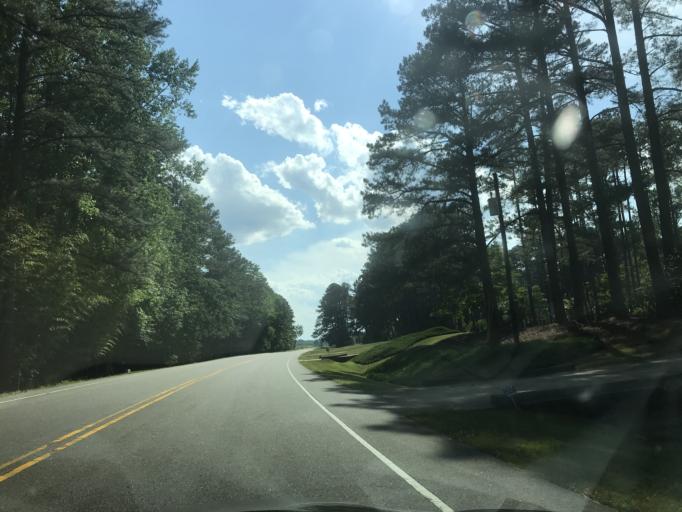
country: US
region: North Carolina
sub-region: Nash County
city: Spring Hope
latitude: 35.9354
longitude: -78.1231
